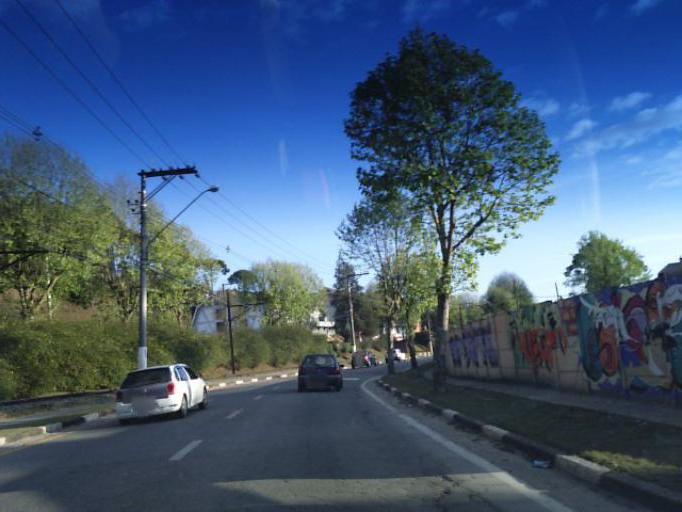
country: BR
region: Sao Paulo
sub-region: Campos Do Jordao
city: Campos do Jordao
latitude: -22.7276
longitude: -45.5816
